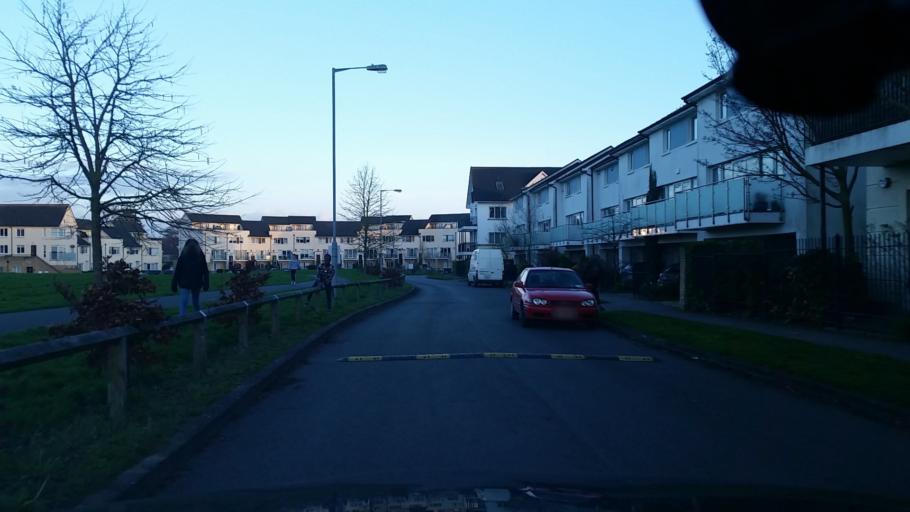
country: IE
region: Leinster
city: Hartstown
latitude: 53.3938
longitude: -6.4355
